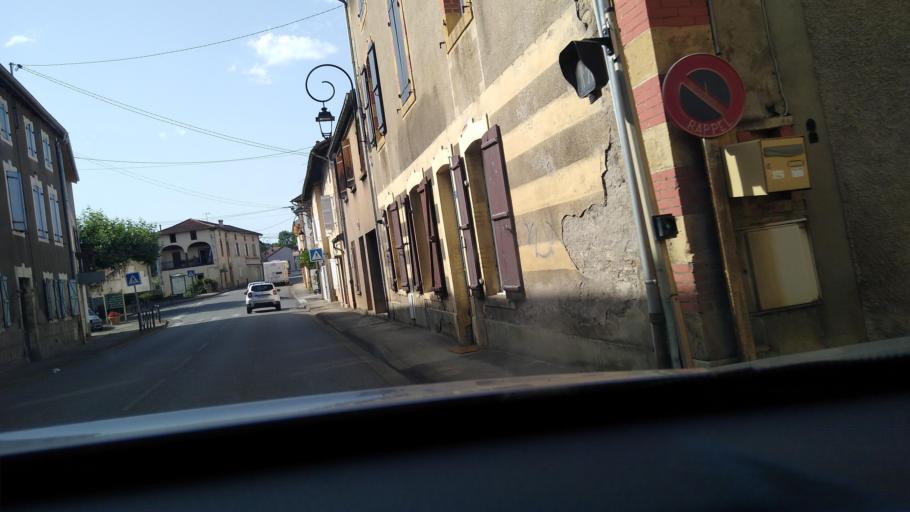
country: FR
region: Midi-Pyrenees
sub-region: Departement de la Haute-Garonne
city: Salies-du-Salat
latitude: 43.0812
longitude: 0.9527
